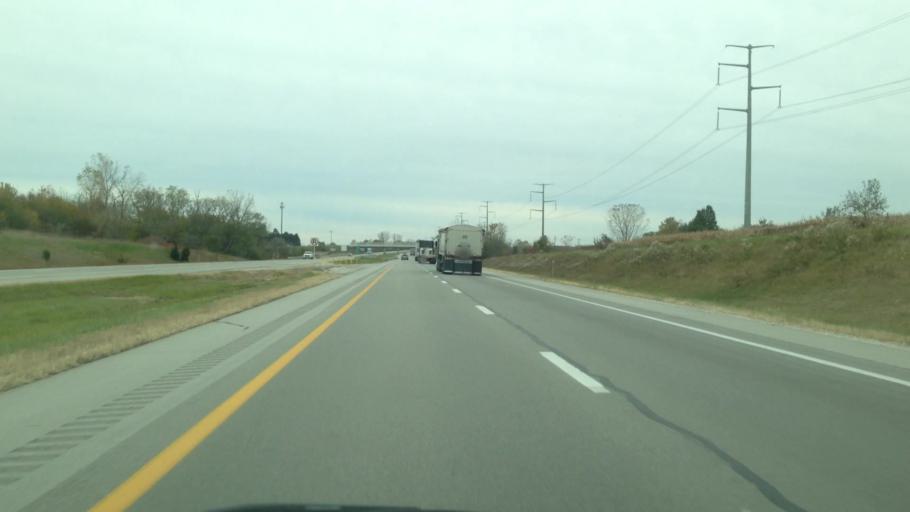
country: US
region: Ohio
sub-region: Fulton County
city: Delta
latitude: 41.5971
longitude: -84.0155
